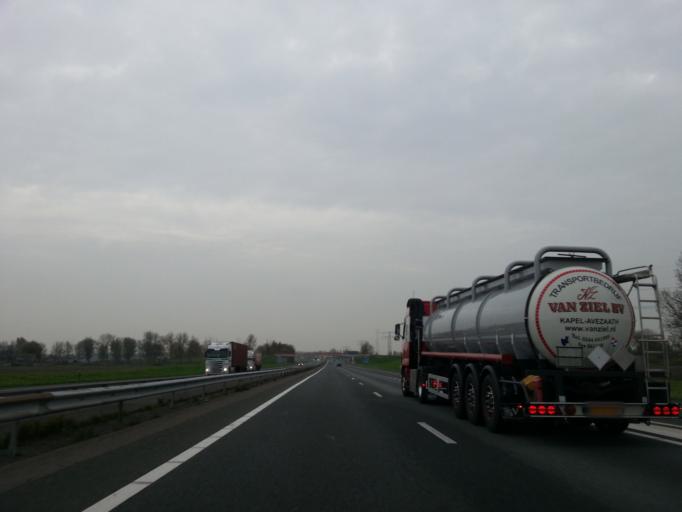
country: NL
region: North Brabant
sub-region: Gemeente Moerdijk
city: Willemstad
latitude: 51.7464
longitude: 4.4138
